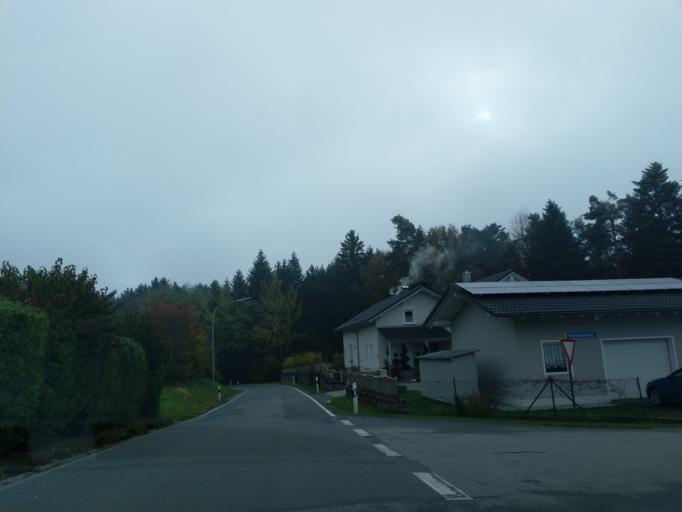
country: DE
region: Bavaria
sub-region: Lower Bavaria
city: Auerbach
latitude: 48.7923
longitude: 13.1036
